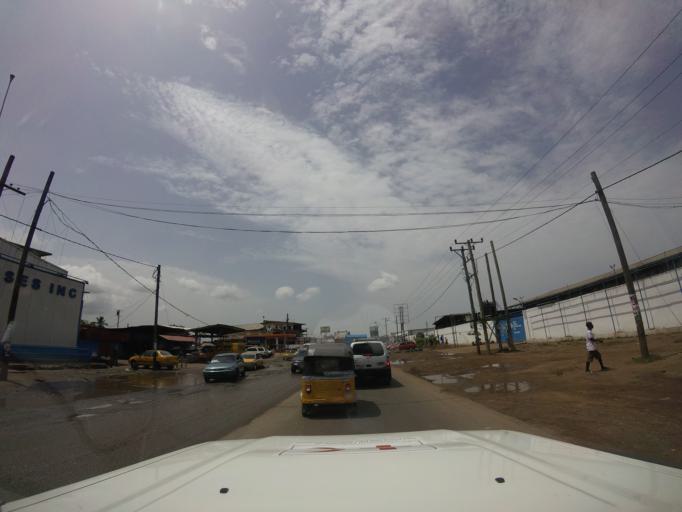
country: LR
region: Montserrado
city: Monrovia
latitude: 6.3542
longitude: -10.7866
